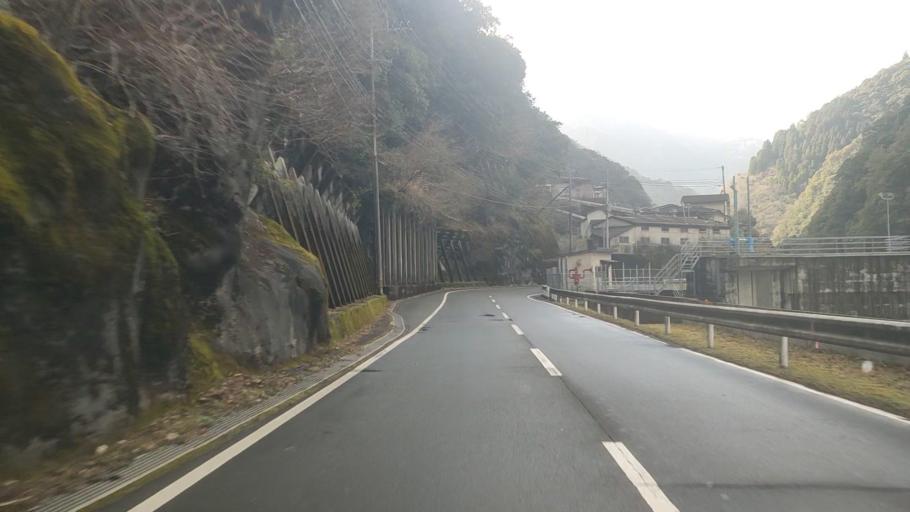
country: JP
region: Kumamoto
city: Hitoyoshi
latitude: 32.4280
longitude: 130.8583
